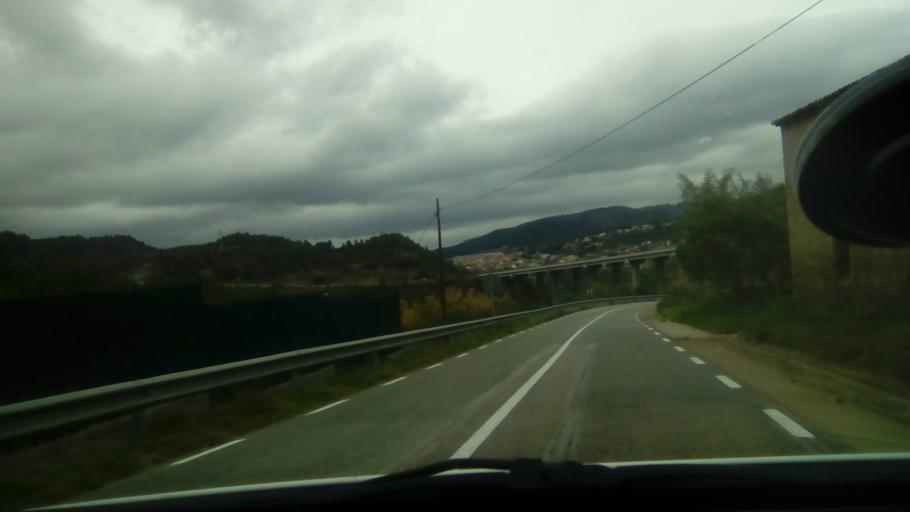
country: ES
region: Catalonia
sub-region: Provincia de Barcelona
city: Manresa
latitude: 41.6853
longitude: 1.8680
